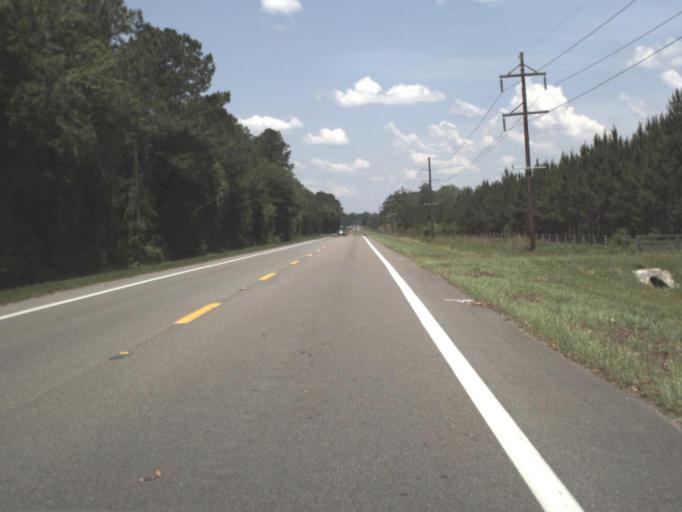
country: US
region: Florida
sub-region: Union County
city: Lake Butler
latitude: 30.0150
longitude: -82.3077
